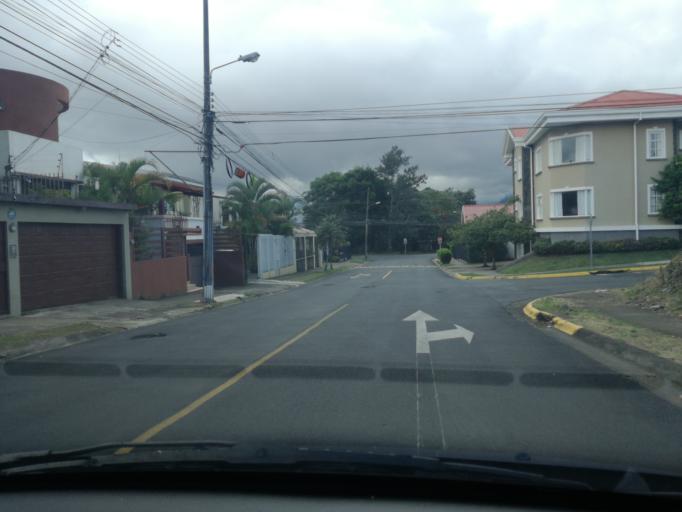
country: CR
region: San Jose
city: San Pedro
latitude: 9.9229
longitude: -84.0440
